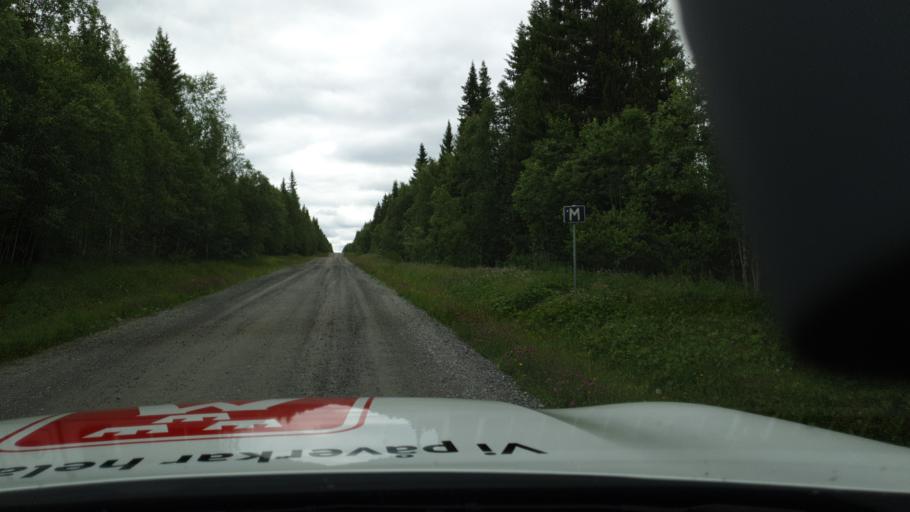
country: SE
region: Vaesterbotten
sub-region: Storumans Kommun
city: Storuman
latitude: 64.7835
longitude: 17.0295
